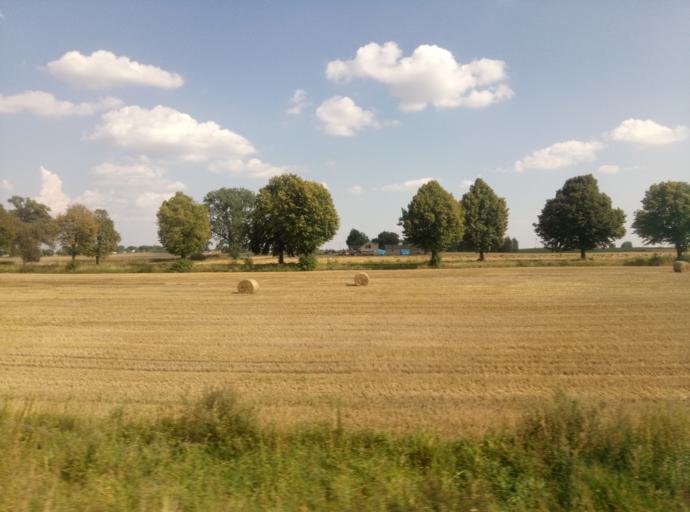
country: PL
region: Kujawsko-Pomorskie
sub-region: Powiat golubsko-dobrzynski
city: Kowalewo Pomorskie
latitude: 53.2109
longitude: 18.9242
